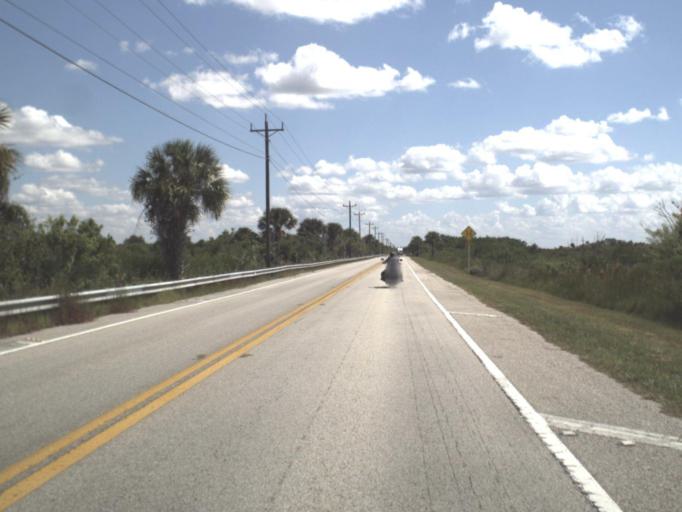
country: US
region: Florida
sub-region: Collier County
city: Marco
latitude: 25.9548
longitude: -81.4873
